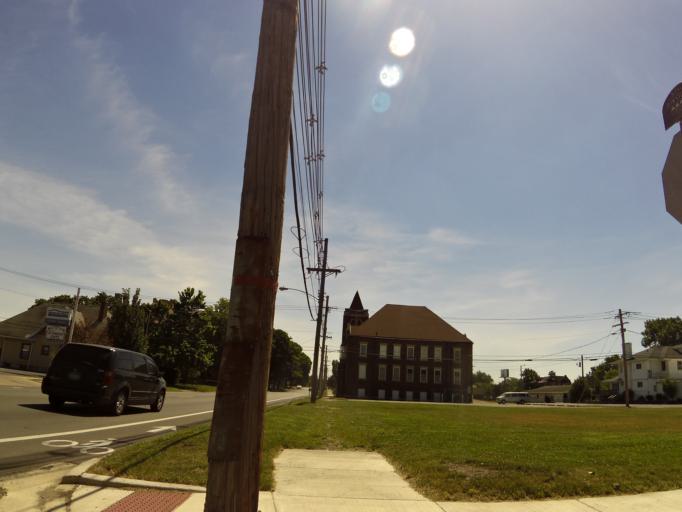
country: US
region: Illinois
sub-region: Vermilion County
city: Danville
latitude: 40.1333
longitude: -87.6327
